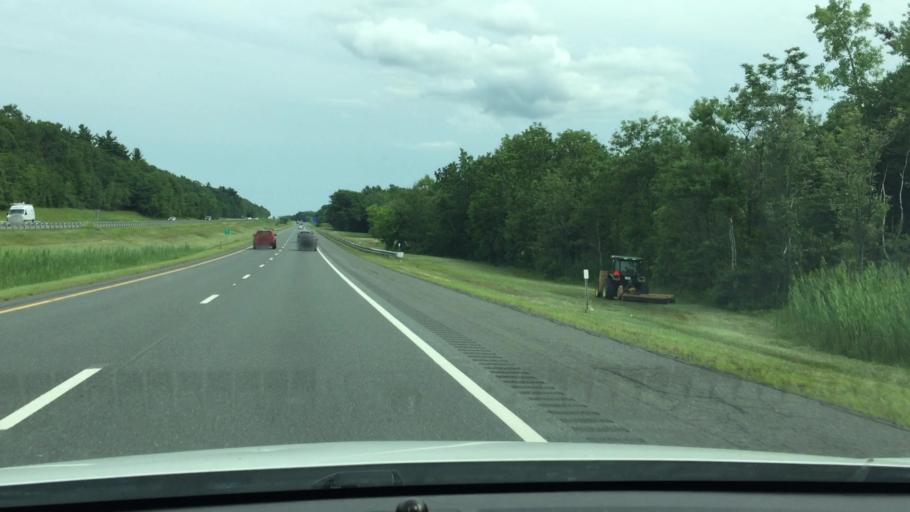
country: US
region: Massachusetts
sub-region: Berkshire County
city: Otis
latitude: 42.2136
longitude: -72.9566
